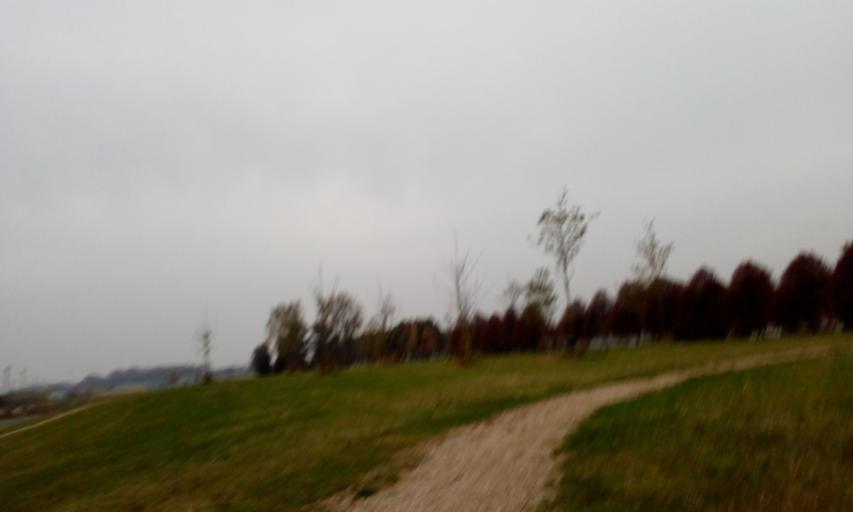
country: NL
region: South Holland
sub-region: Gemeente Lansingerland
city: Berkel en Rodenrijs
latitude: 51.9815
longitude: 4.4728
